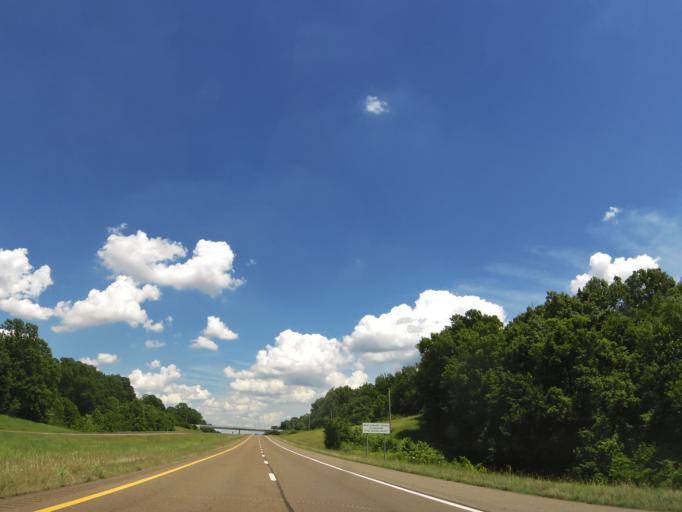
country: US
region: Tennessee
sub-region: Dyer County
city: Dyersburg
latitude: 36.0707
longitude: -89.4568
